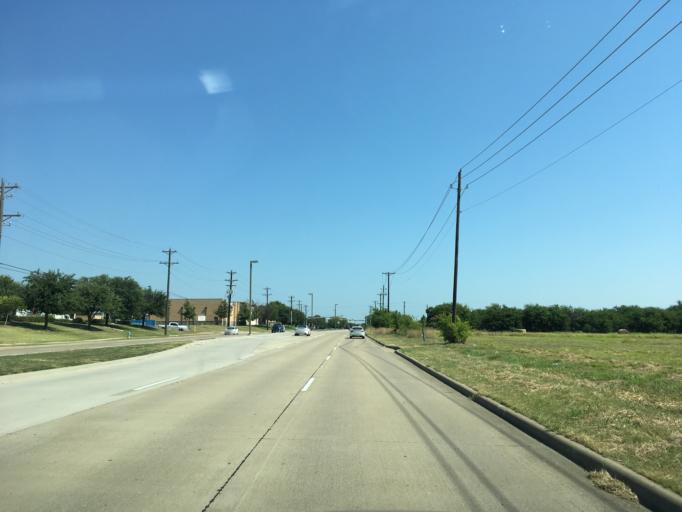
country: US
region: Texas
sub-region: Collin County
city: Fairview
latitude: 33.1558
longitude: -96.6806
